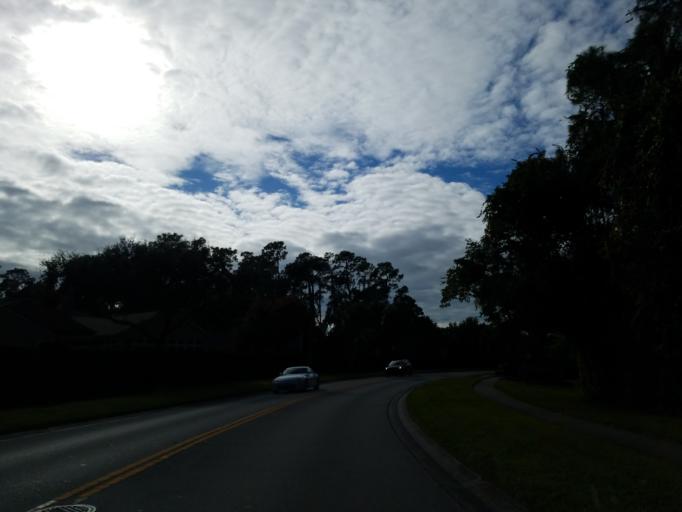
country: US
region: Florida
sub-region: Hillsborough County
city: Bloomingdale
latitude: 27.8848
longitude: -82.2529
